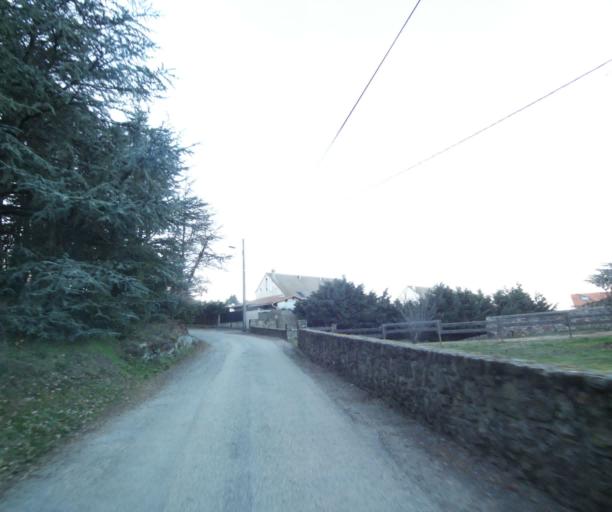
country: FR
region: Rhone-Alpes
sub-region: Departement de l'Ardeche
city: Davezieux
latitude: 45.2529
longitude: 4.7129
